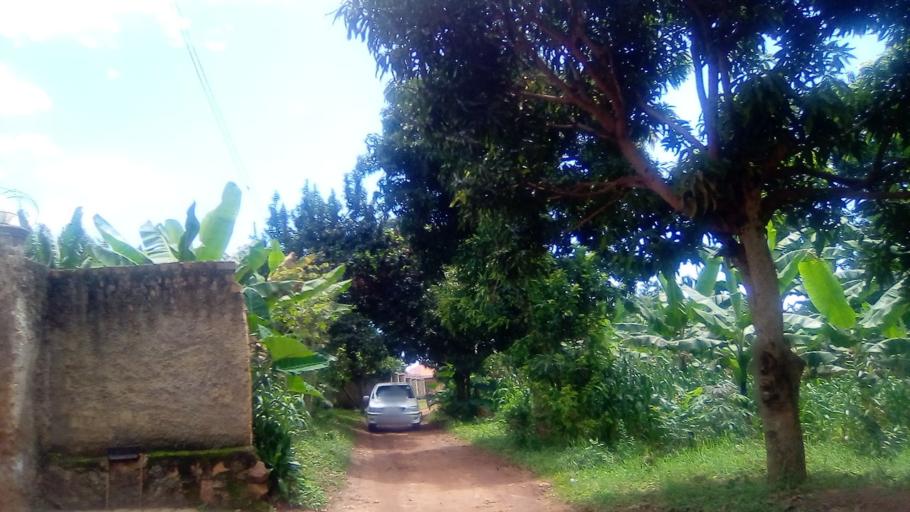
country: UG
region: Central Region
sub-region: Wakiso District
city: Entebbe
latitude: 0.0987
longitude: 32.5289
